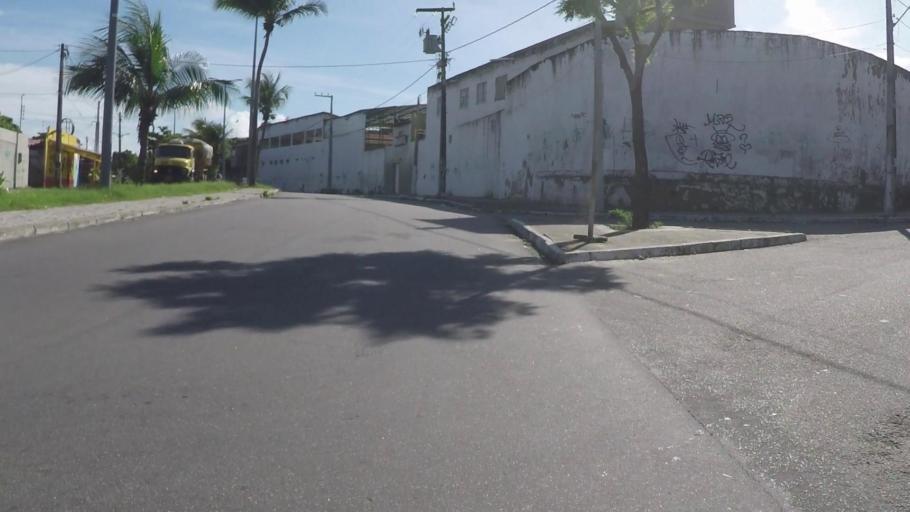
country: BR
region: Ceara
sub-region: Fortaleza
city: Fortaleza
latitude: -3.6994
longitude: -38.5876
